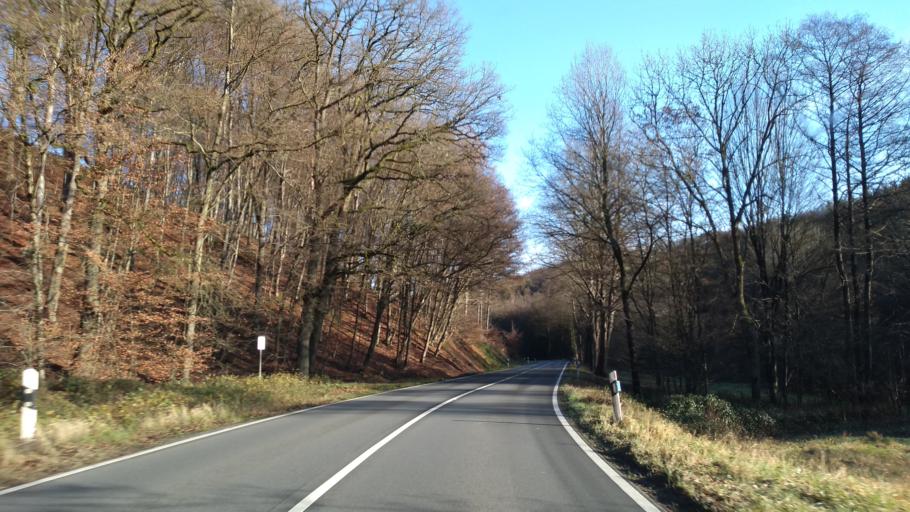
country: DE
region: North Rhine-Westphalia
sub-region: Regierungsbezirk Koln
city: Overath
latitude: 50.8549
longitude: 7.3198
